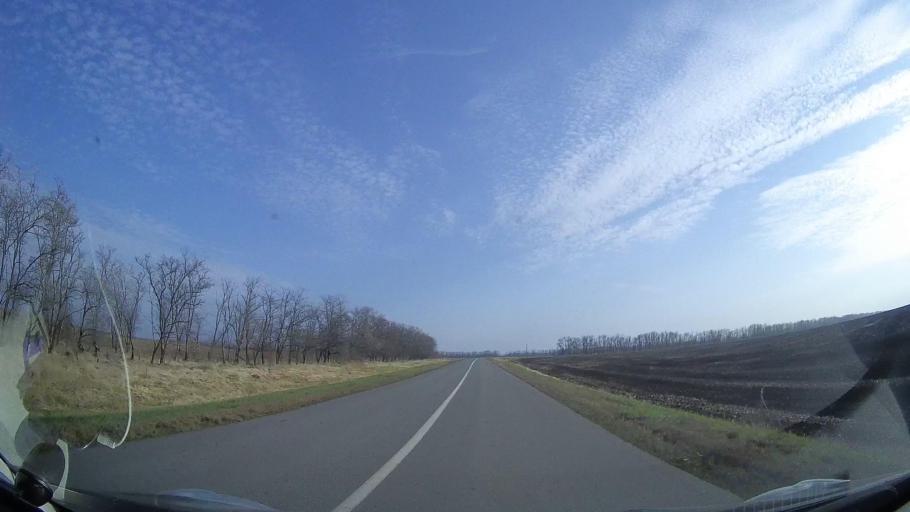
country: RU
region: Rostov
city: Mechetinskaya
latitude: 46.9049
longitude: 40.5380
